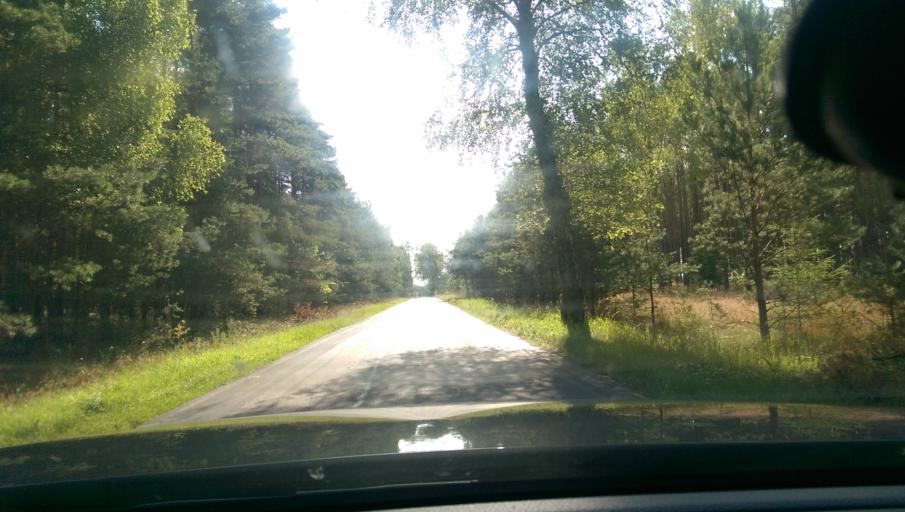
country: PL
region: West Pomeranian Voivodeship
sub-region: Powiat walecki
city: Walcz
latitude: 53.3539
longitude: 16.5500
